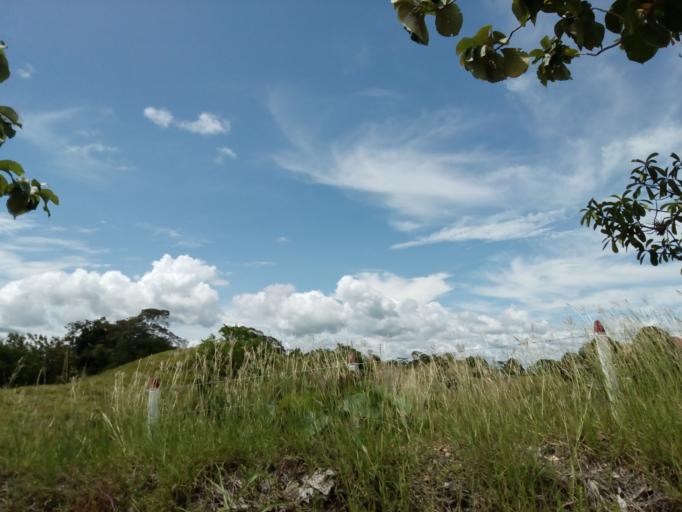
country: CO
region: Boyaca
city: Puerto Boyaca
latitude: 5.9649
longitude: -74.4420
